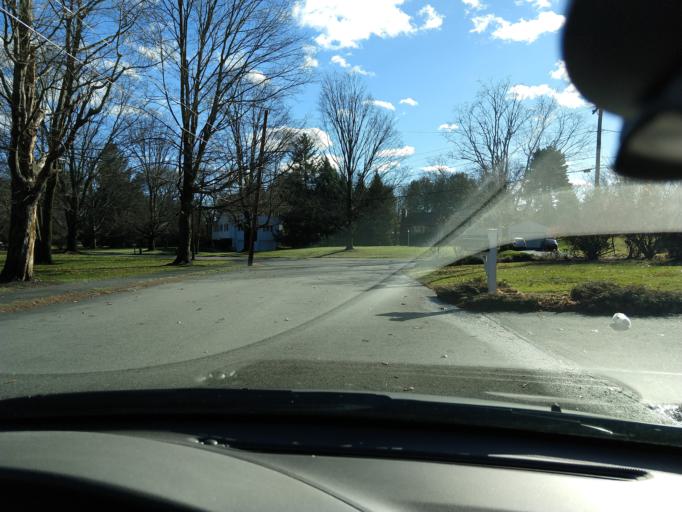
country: US
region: Massachusetts
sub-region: Middlesex County
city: Bedford
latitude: 42.5038
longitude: -71.2590
